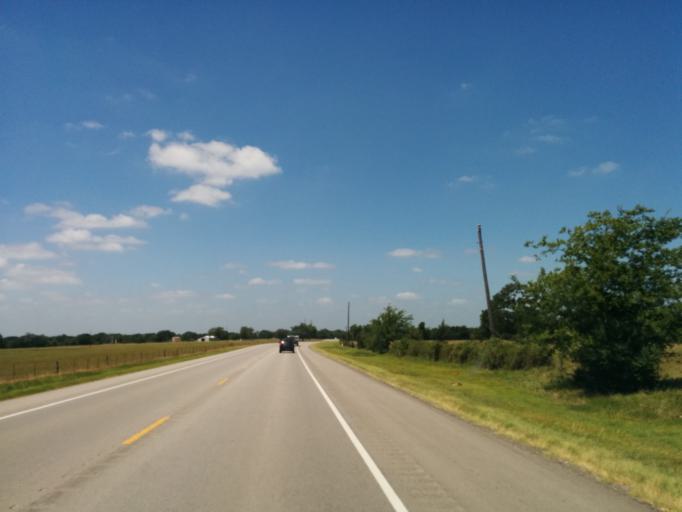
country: US
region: Texas
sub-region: Leon County
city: Hilltop Lakes
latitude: 30.9018
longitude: -96.1368
